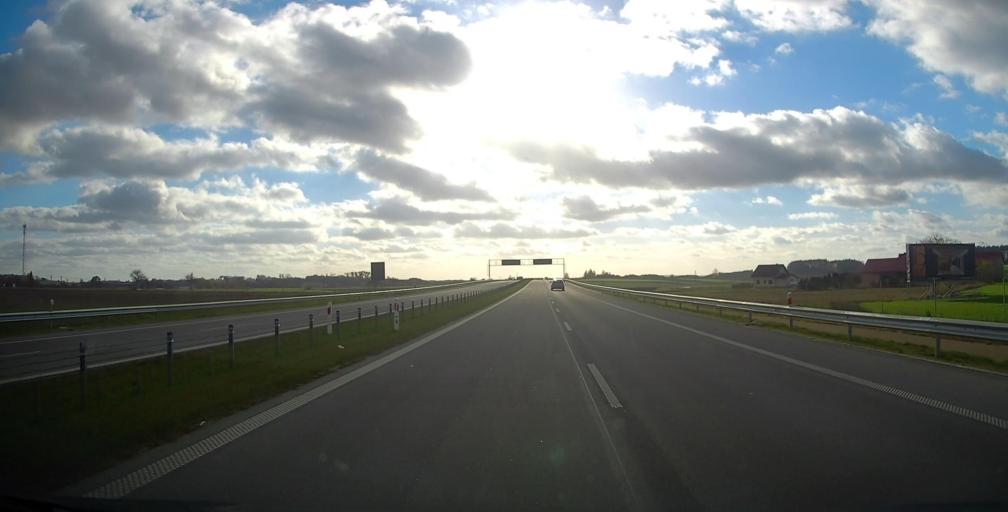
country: PL
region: Podlasie
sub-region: Powiat lomzynski
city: Piatnica
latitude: 53.2634
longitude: 22.1190
